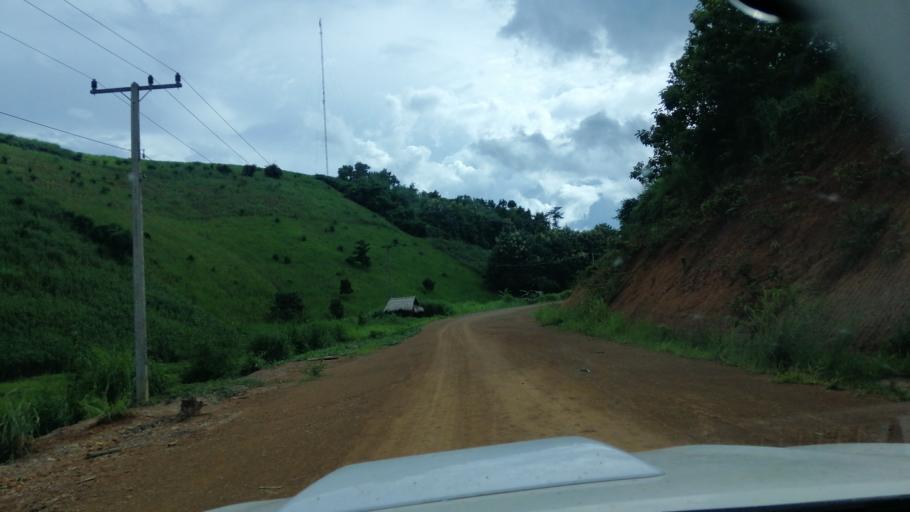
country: TH
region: Nan
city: Song Khwae
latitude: 19.5526
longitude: 100.7020
